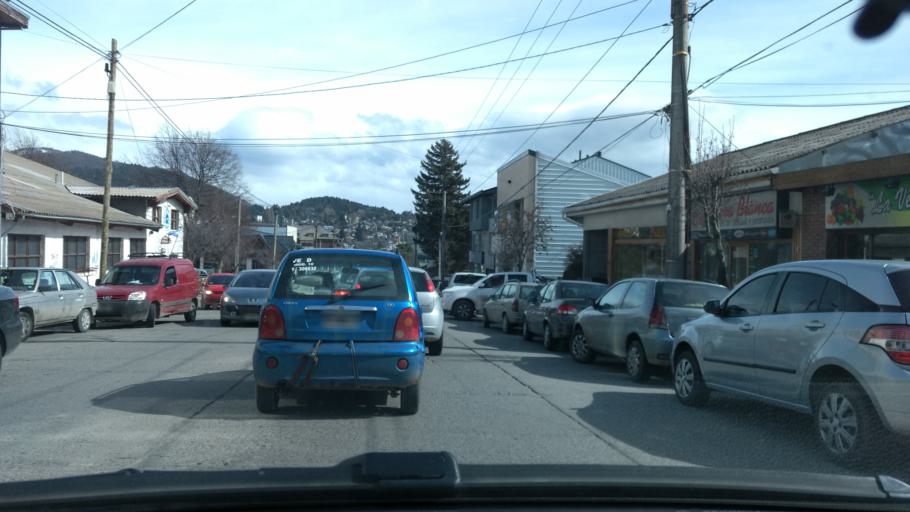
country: AR
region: Rio Negro
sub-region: Departamento de Bariloche
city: San Carlos de Bariloche
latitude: -41.1376
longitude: -71.3022
